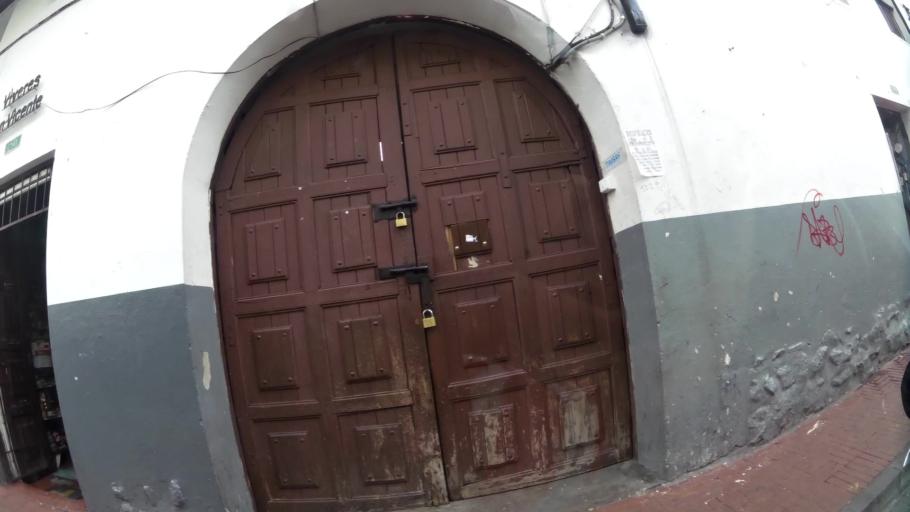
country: EC
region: Pichincha
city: Quito
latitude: -0.2249
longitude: -78.5123
